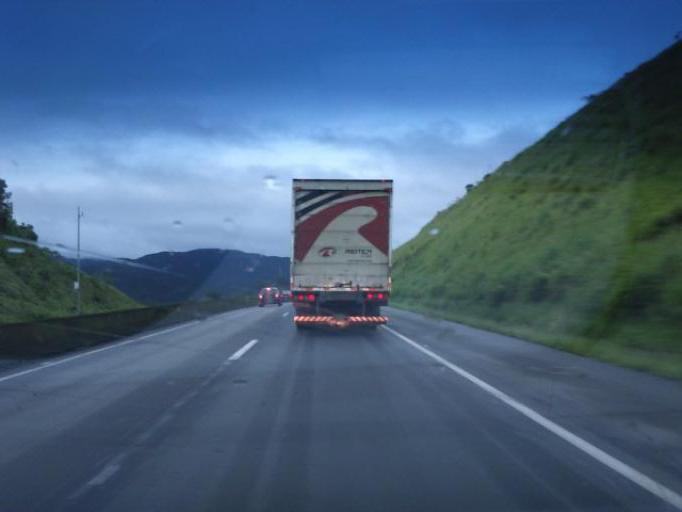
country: BR
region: Sao Paulo
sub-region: Miracatu
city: Miracatu
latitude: -24.1695
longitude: -47.3379
